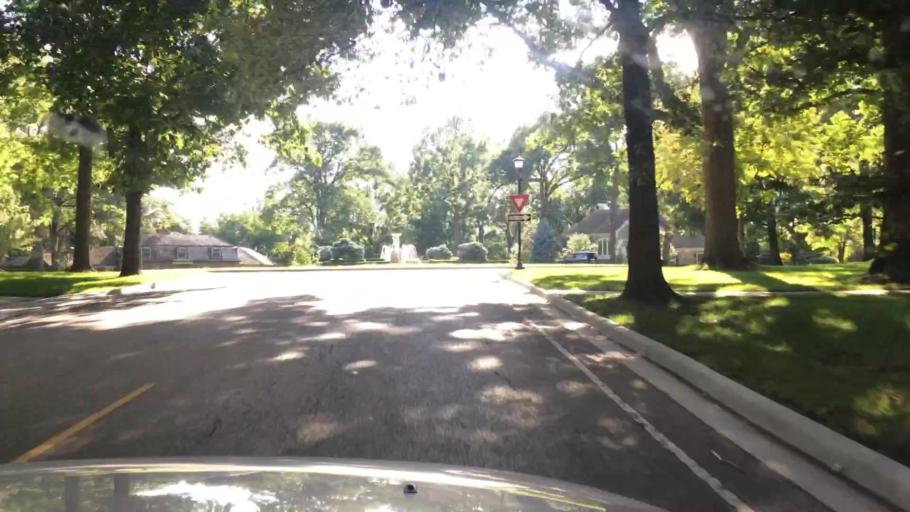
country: US
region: Kansas
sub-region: Johnson County
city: Mission Hills
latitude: 39.0130
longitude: -94.6152
